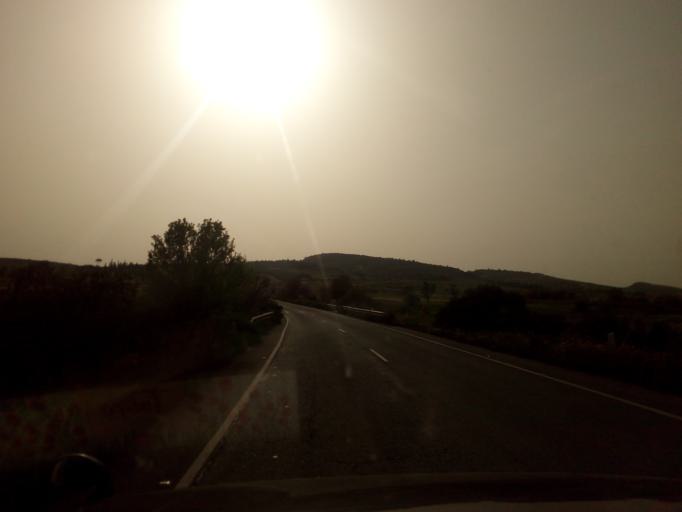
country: CY
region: Lefkosia
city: Lympia
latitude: 35.0012
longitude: 33.4929
